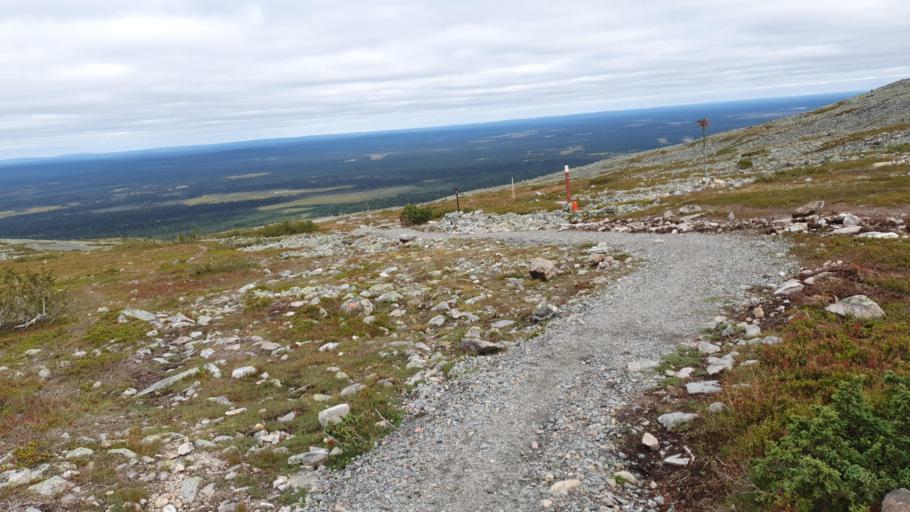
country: FI
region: Lapland
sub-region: Tunturi-Lappi
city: Kolari
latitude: 67.5686
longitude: 24.2371
